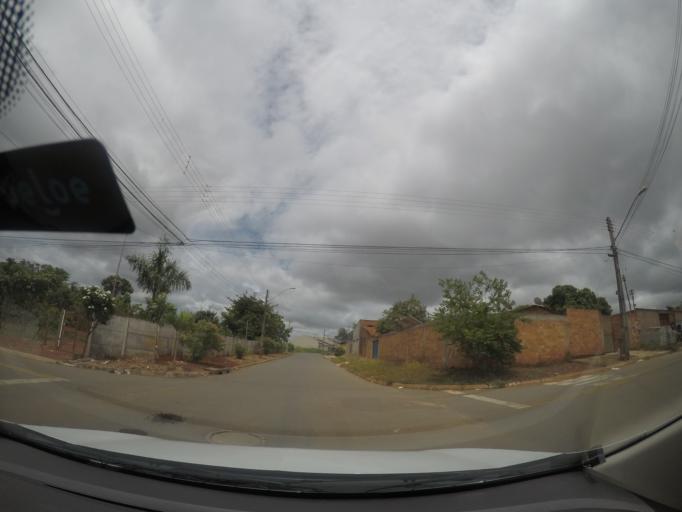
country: BR
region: Goias
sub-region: Goiania
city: Goiania
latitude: -16.7221
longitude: -49.3596
